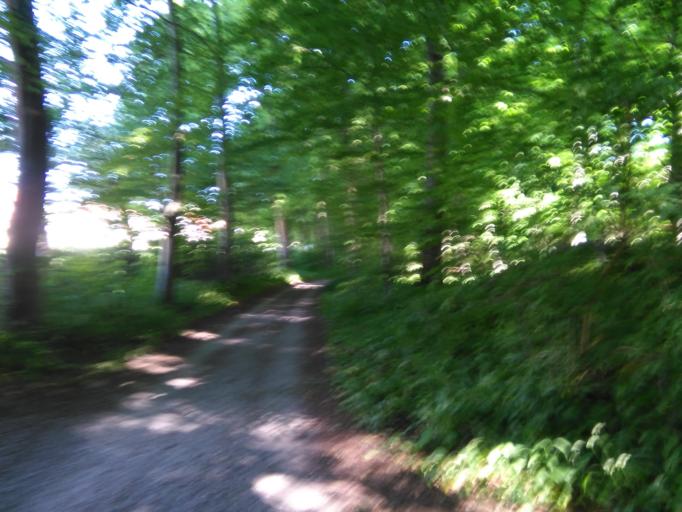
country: DK
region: Central Jutland
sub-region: Arhus Kommune
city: Arhus
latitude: 56.1756
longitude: 10.2216
